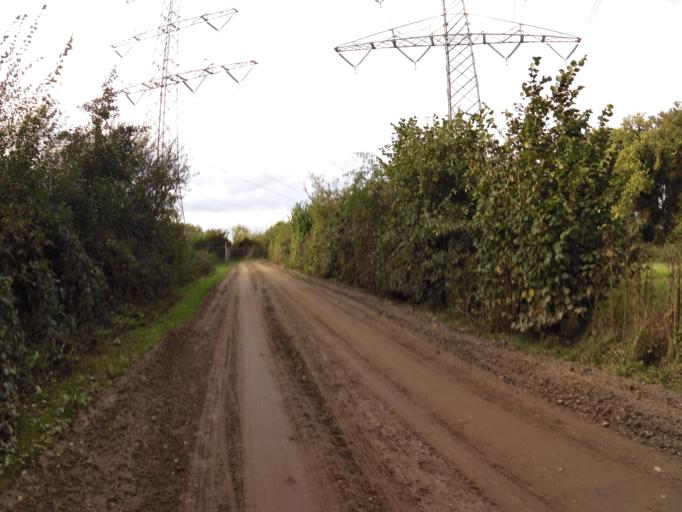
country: NL
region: Limburg
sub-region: Gemeente Maasgouw
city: Maasbracht
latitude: 51.1559
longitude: 5.9191
